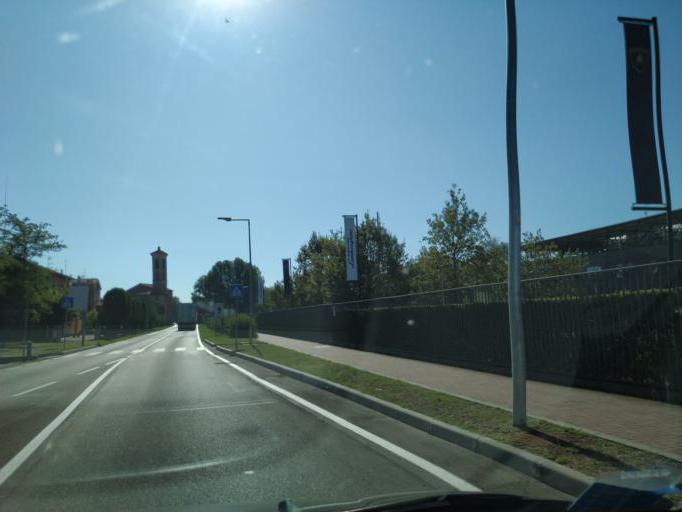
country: IT
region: Emilia-Romagna
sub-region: Provincia di Bologna
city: Sant'Agata Bolognese
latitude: 44.6594
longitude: 11.1268
